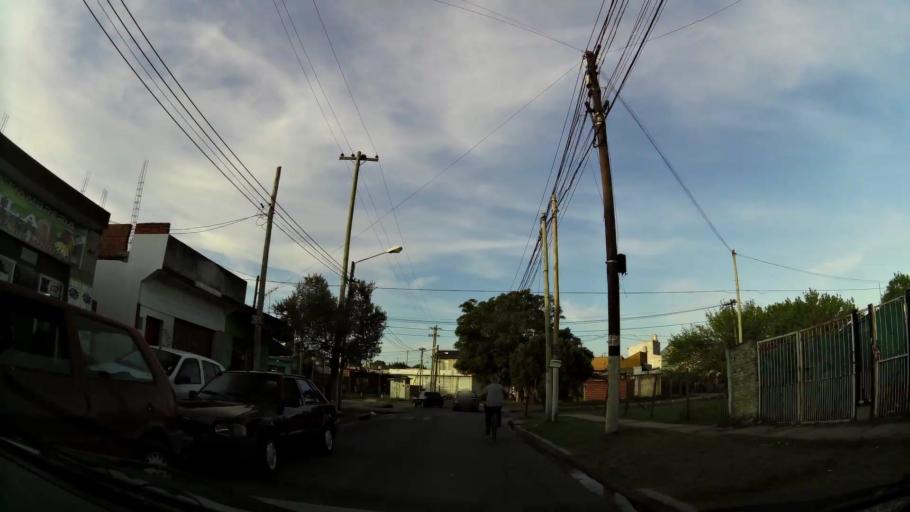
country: AR
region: Buenos Aires
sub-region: Partido de Quilmes
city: Quilmes
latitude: -34.7762
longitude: -58.1981
